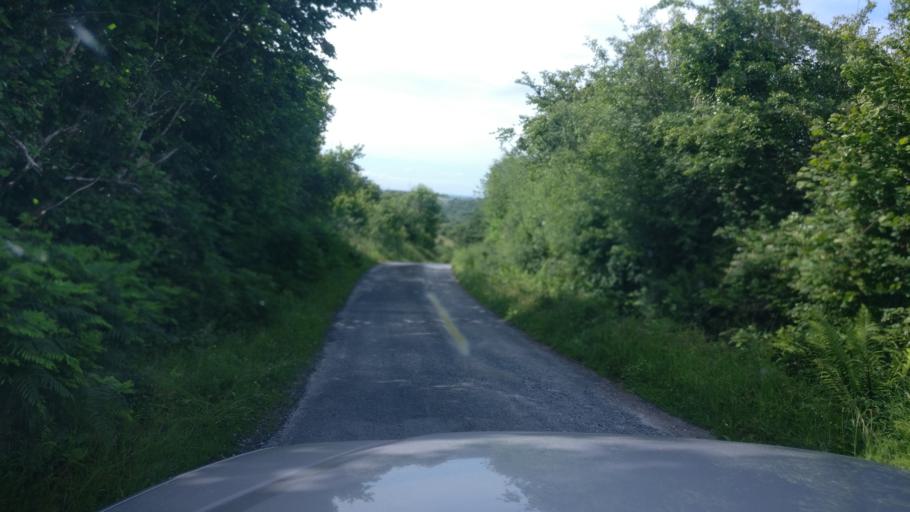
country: IE
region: Connaught
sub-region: County Galway
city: Gort
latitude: 53.0925
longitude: -8.6978
